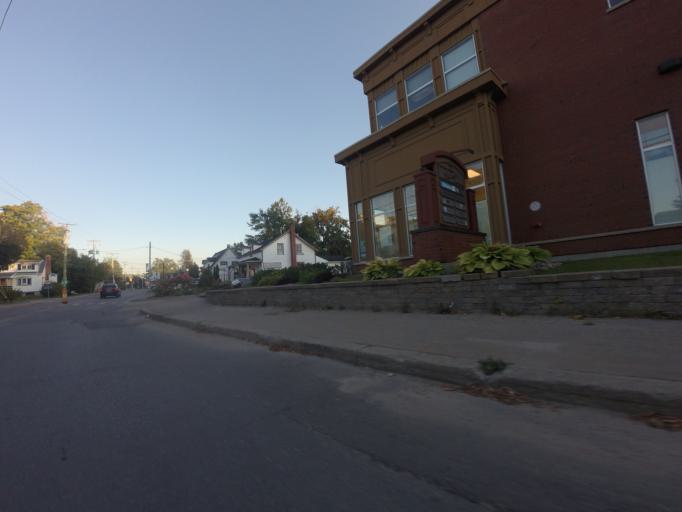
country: CA
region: Quebec
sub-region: Monteregie
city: Hudson
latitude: 45.4587
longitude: -74.1413
